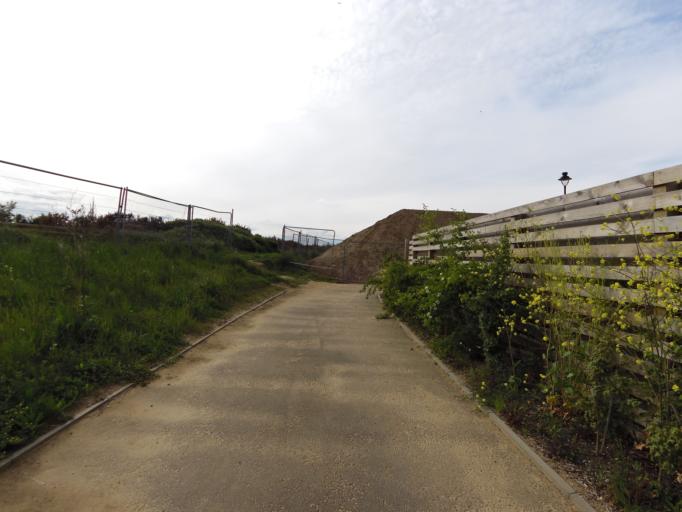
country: GB
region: England
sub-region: Suffolk
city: Ipswich
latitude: 52.0258
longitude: 1.1908
